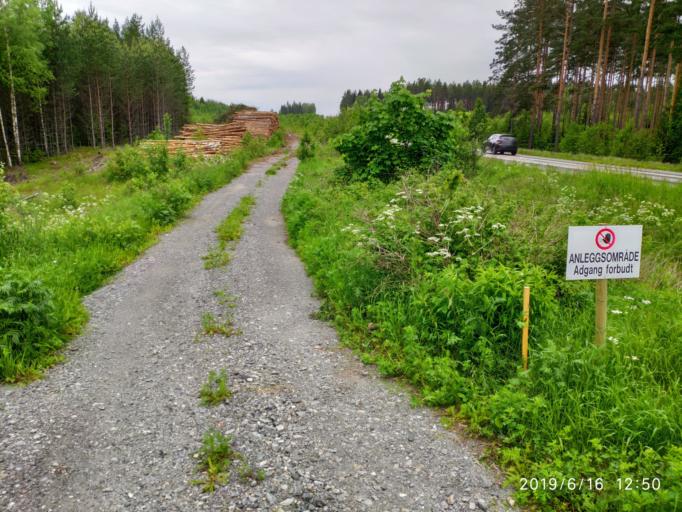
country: NO
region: Oppland
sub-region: Jevnaker
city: Jevnaker
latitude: 60.2223
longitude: 10.3469
